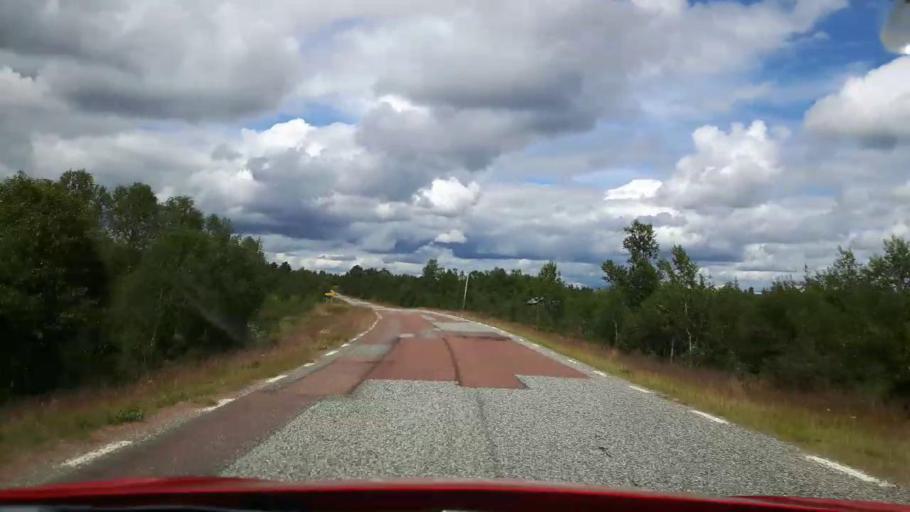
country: NO
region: Hedmark
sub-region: Trysil
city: Innbygda
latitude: 62.1041
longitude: 12.9831
